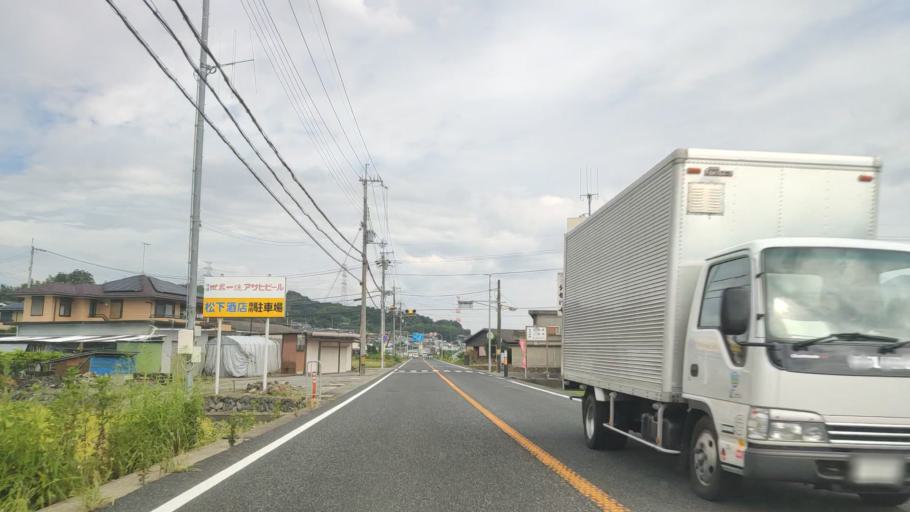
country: JP
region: Wakayama
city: Iwade
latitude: 34.2767
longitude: 135.4439
